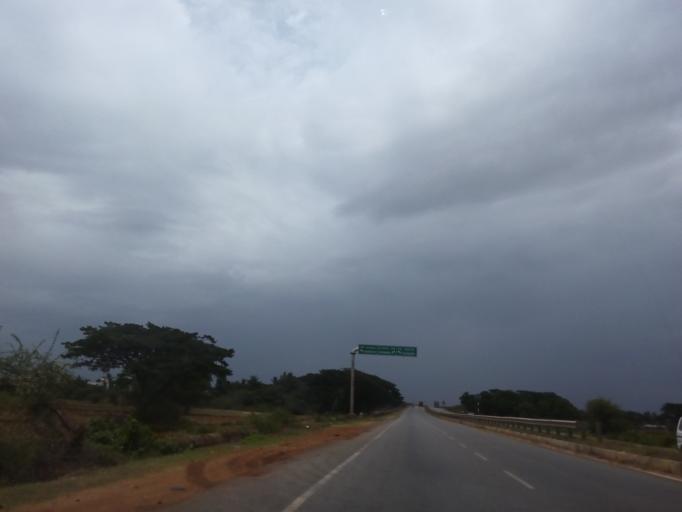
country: IN
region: Karnataka
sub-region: Davanagere
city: Harihar
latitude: 14.4715
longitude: 75.8315
